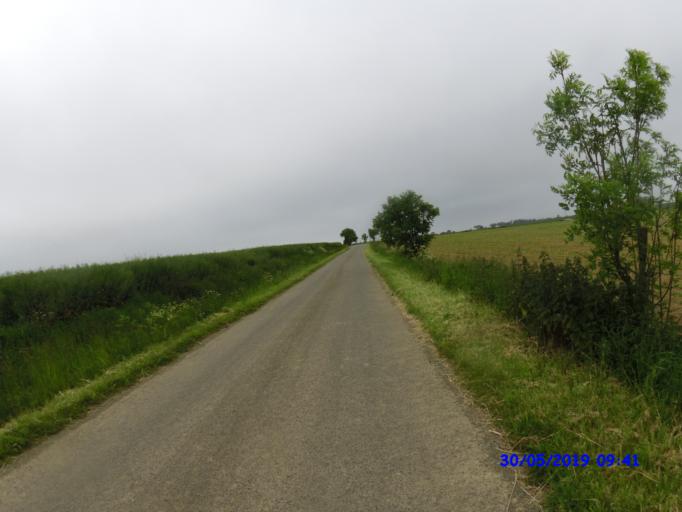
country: BE
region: Wallonia
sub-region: Province du Hainaut
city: Beaumont
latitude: 50.2436
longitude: 4.2737
